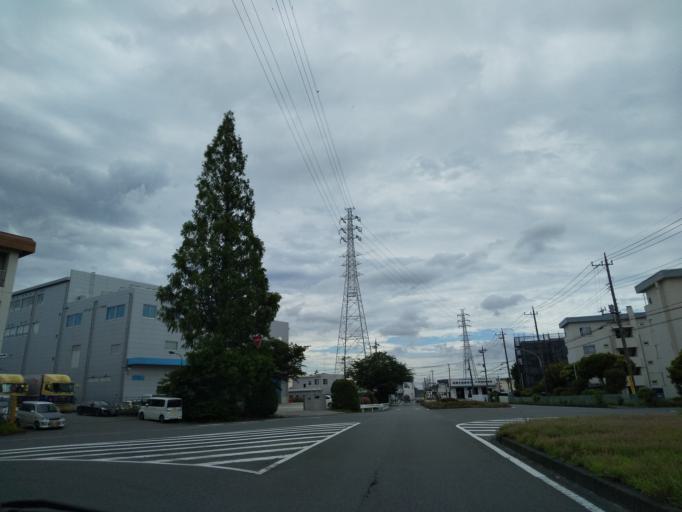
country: JP
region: Kanagawa
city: Zama
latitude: 35.5092
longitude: 139.3455
